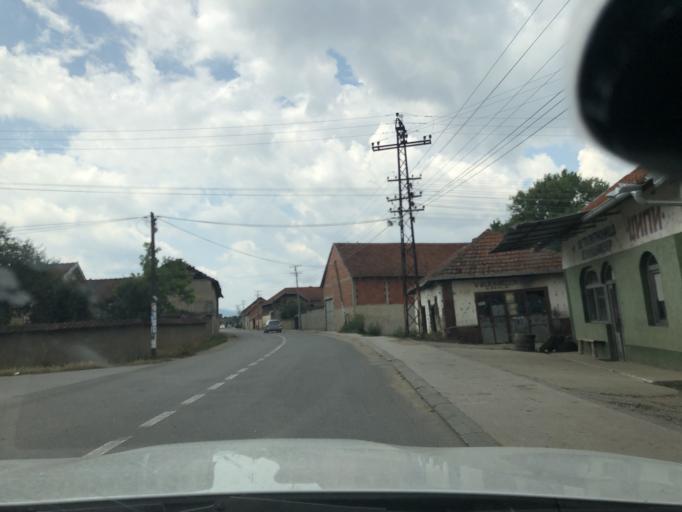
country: RS
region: Central Serbia
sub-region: Jablanicki Okrug
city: Lebane
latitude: 42.9469
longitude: 21.8262
